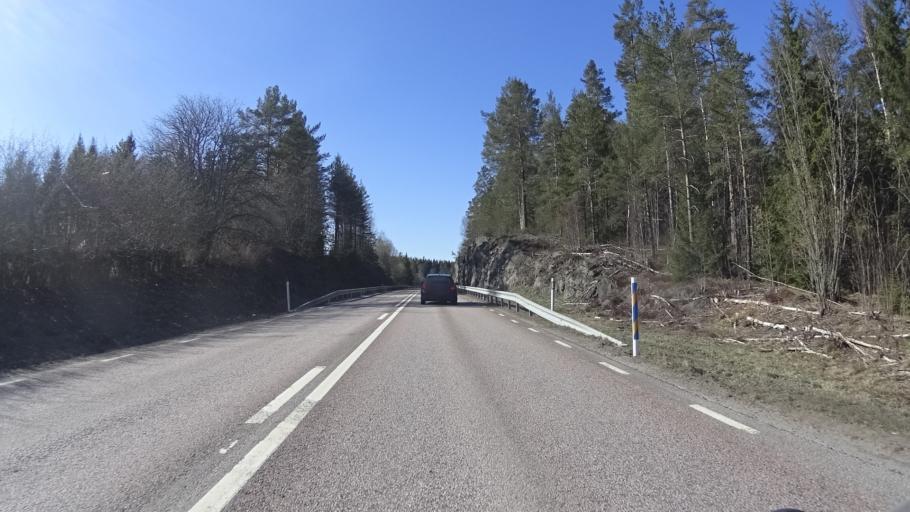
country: SE
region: Vaermland
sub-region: Karlstads Kommun
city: Edsvalla
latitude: 59.5438
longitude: 13.0739
